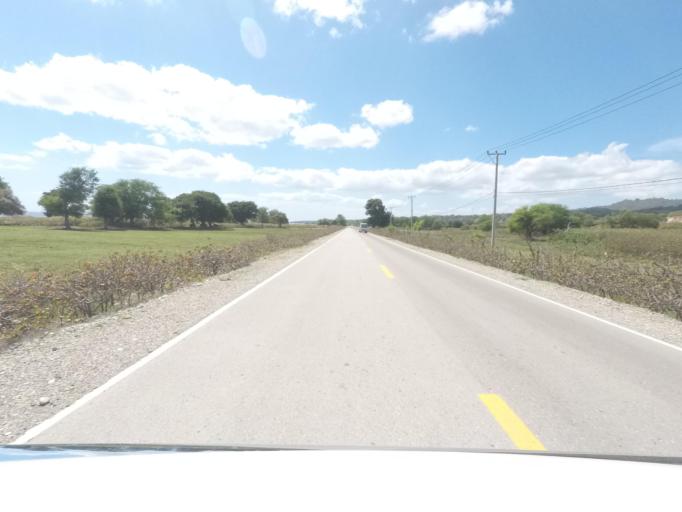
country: TL
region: Baucau
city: Baucau
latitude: -8.4538
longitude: 126.6294
